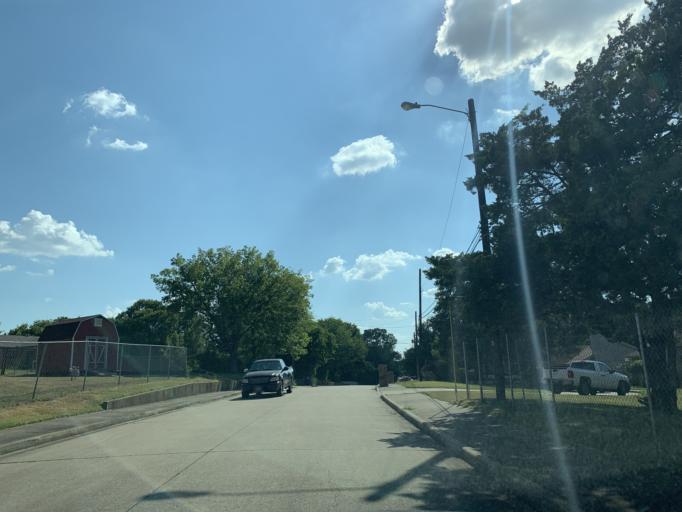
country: US
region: Texas
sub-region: Dallas County
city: Hutchins
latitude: 32.6584
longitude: -96.7788
